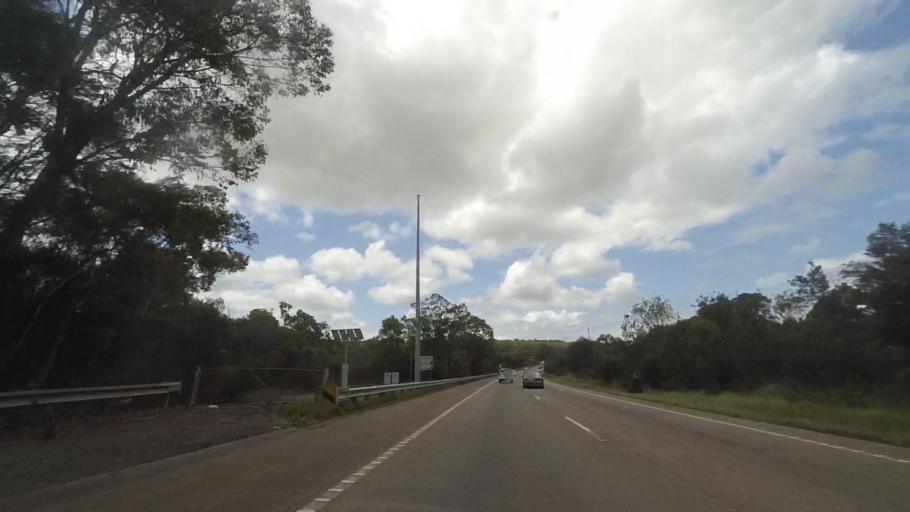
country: AU
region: New South Wales
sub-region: Gosford Shire
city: Narara
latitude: -33.3809
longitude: 151.2996
